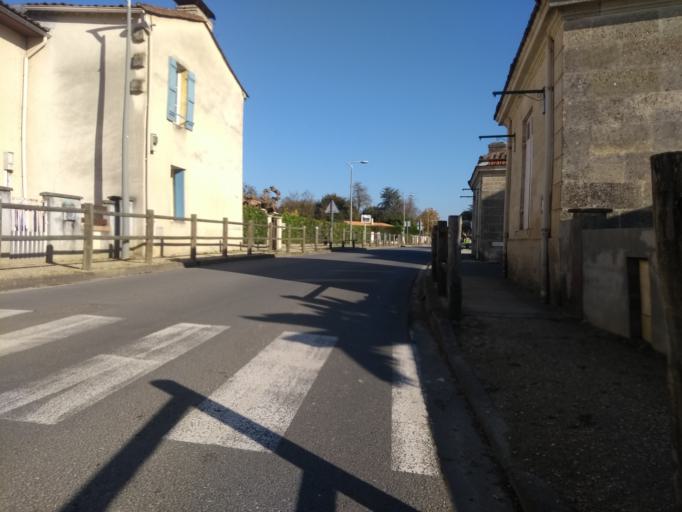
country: FR
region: Aquitaine
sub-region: Departement de la Gironde
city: Ayguemorte-les-Graves
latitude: 44.7104
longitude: -0.4798
